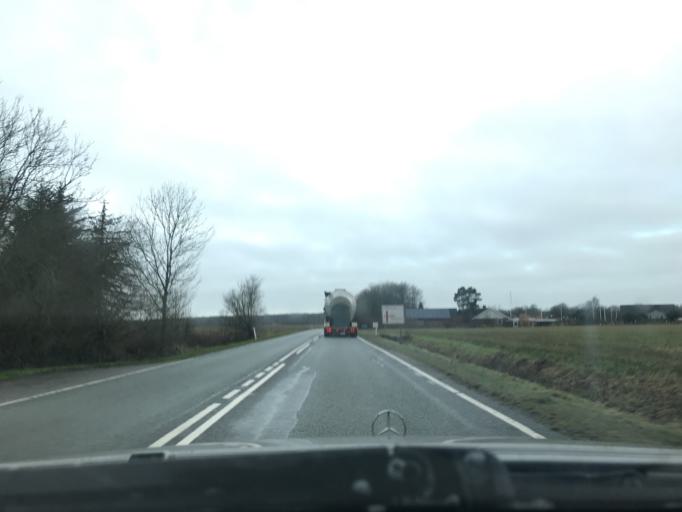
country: DK
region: South Denmark
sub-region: Haderslev Kommune
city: Gram
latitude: 55.2532
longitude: 8.9112
